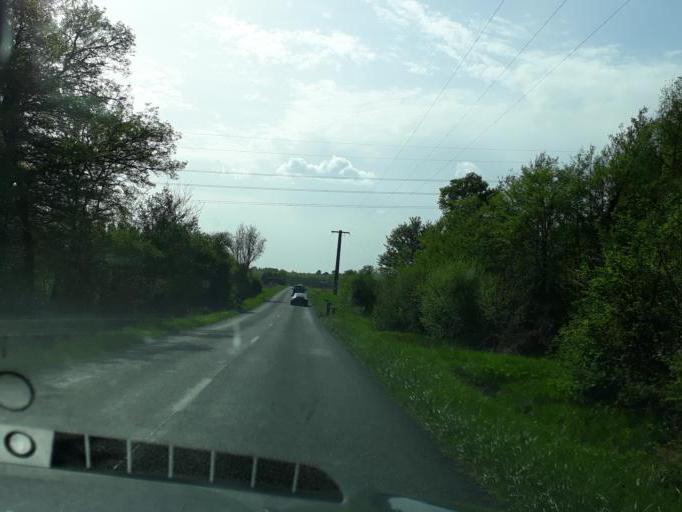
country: FR
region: Centre
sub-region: Departement du Loir-et-Cher
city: Dhuizon
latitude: 47.6575
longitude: 1.6426
